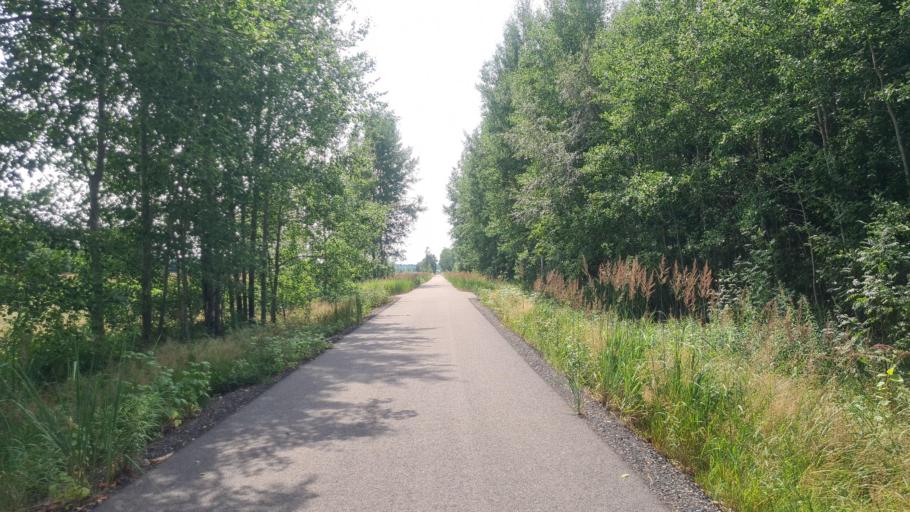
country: SE
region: Kronoberg
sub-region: Ljungby Kommun
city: Lagan
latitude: 56.8895
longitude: 13.9846
